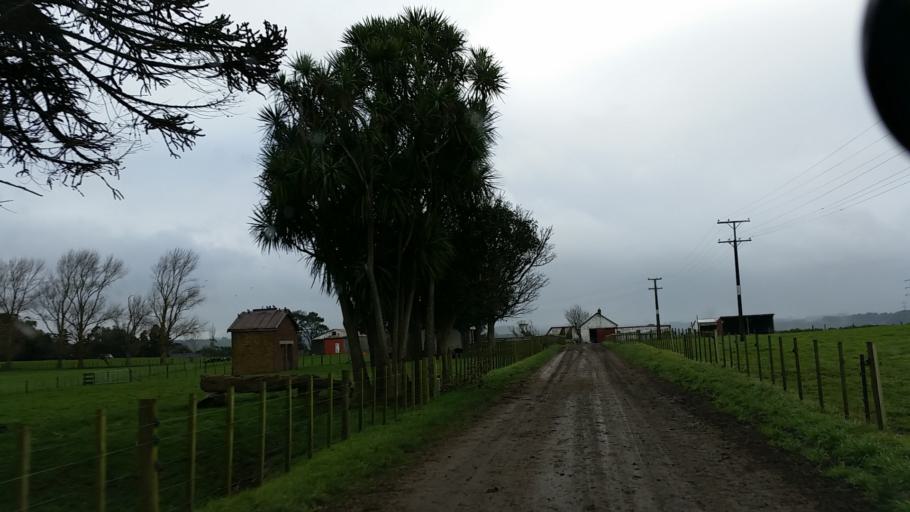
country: NZ
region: Taranaki
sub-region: South Taranaki District
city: Patea
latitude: -39.7695
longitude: 174.7089
